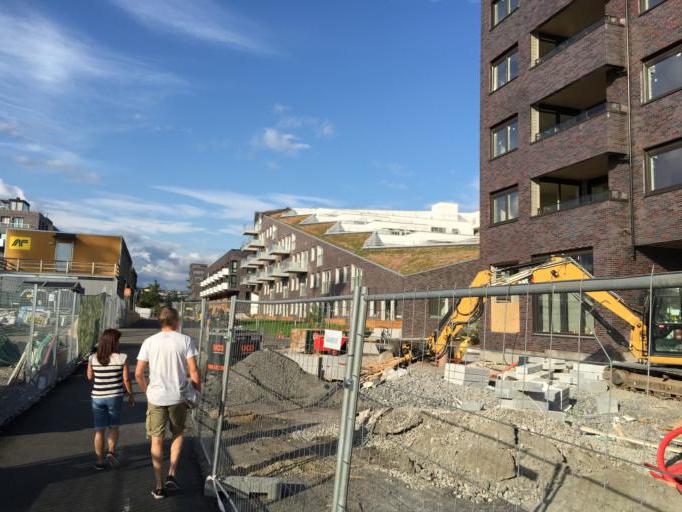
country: NO
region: Oslo
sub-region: Oslo
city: Oslo
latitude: 59.9013
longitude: 10.7520
